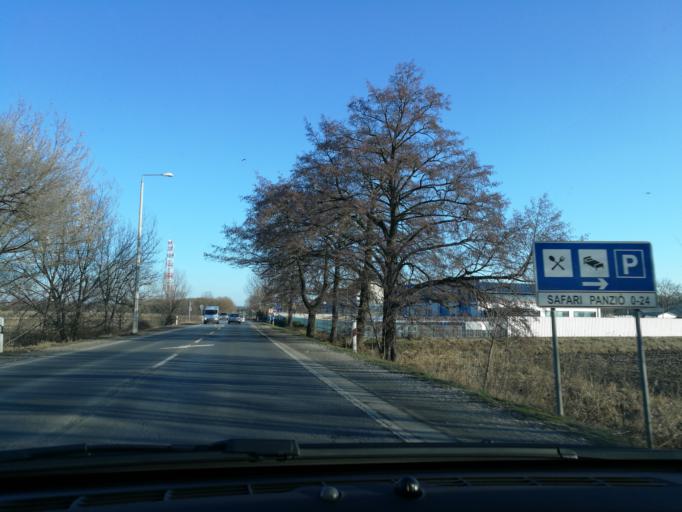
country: HU
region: Szabolcs-Szatmar-Bereg
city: Nyirpazony
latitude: 47.9492
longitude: 21.7899
